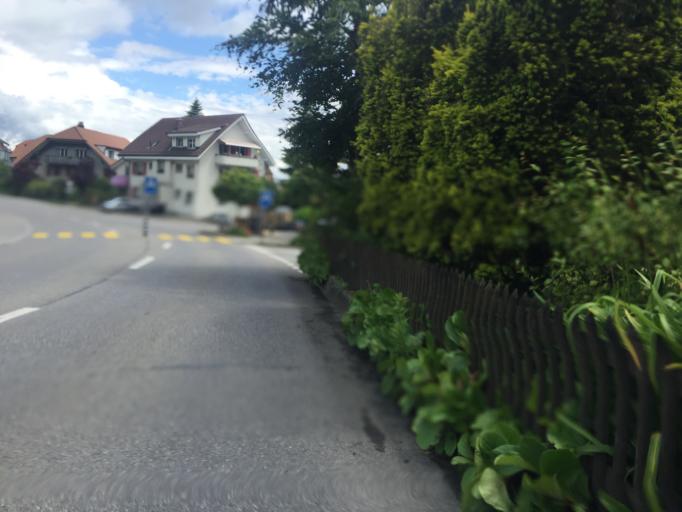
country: CH
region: Bern
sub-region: Bern-Mittelland District
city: Wohlen
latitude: 46.9864
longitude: 7.3844
